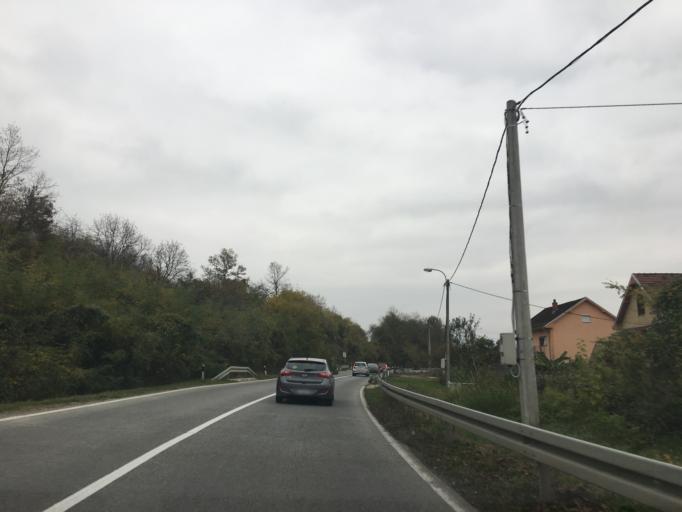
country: RS
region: Central Serbia
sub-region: Raski Okrug
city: Kraljevo
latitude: 43.7159
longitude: 20.7843
